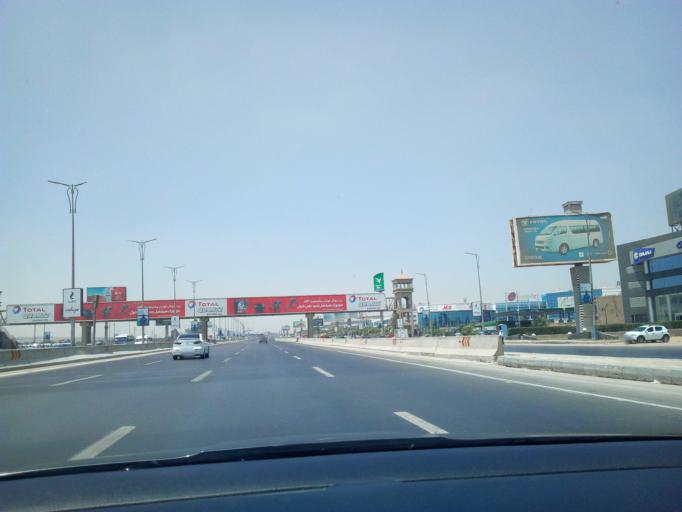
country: EG
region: Al Jizah
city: Awsim
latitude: 30.0601
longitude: 31.0307
